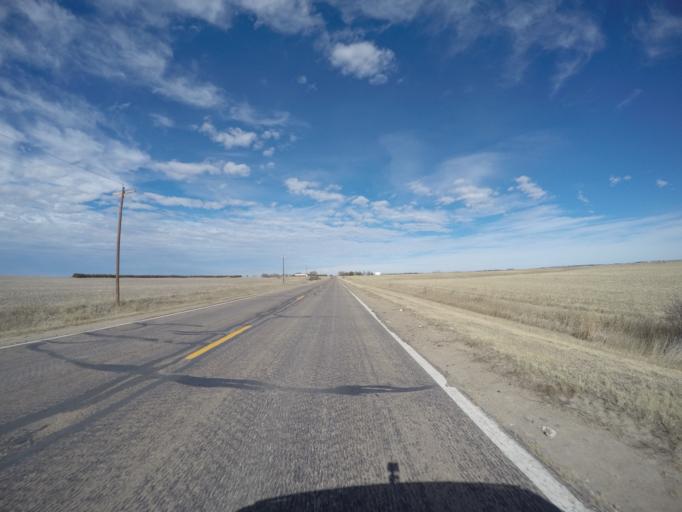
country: US
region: Nebraska
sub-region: Franklin County
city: Franklin
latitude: 40.2785
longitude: -98.9524
